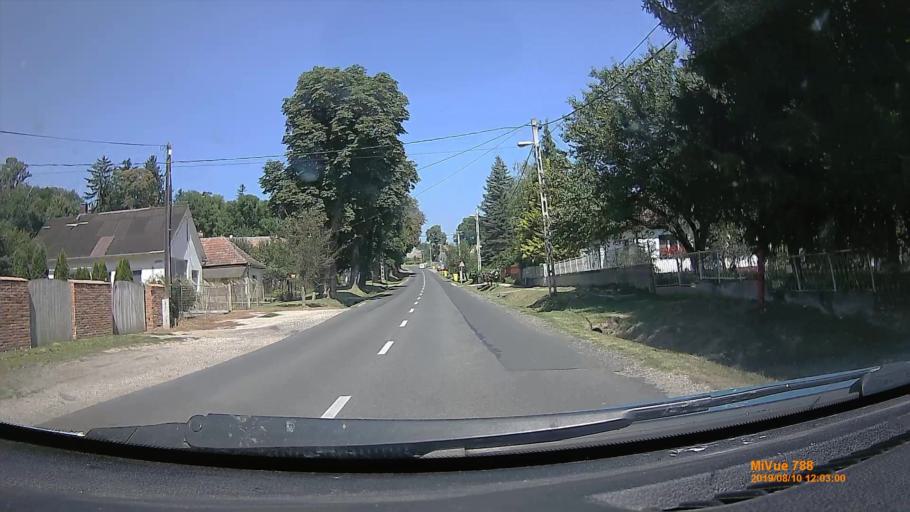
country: HU
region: Somogy
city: Somogyvar
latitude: 46.5776
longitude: 17.6497
